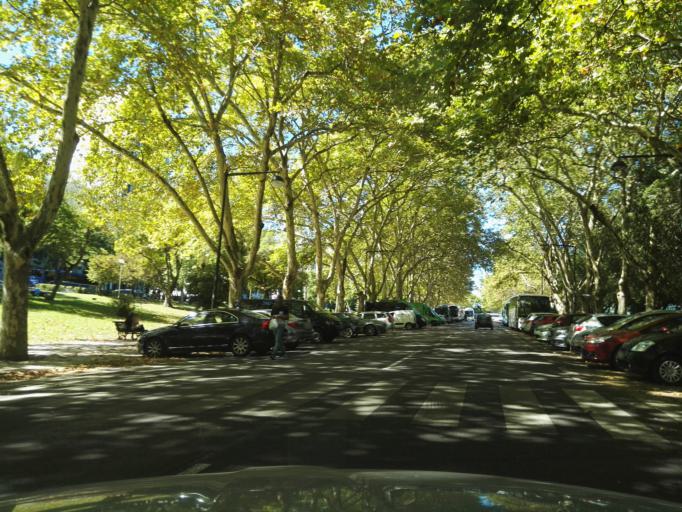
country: PT
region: Lisbon
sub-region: Lisbon
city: Lisbon
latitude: 38.7279
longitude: -9.1552
